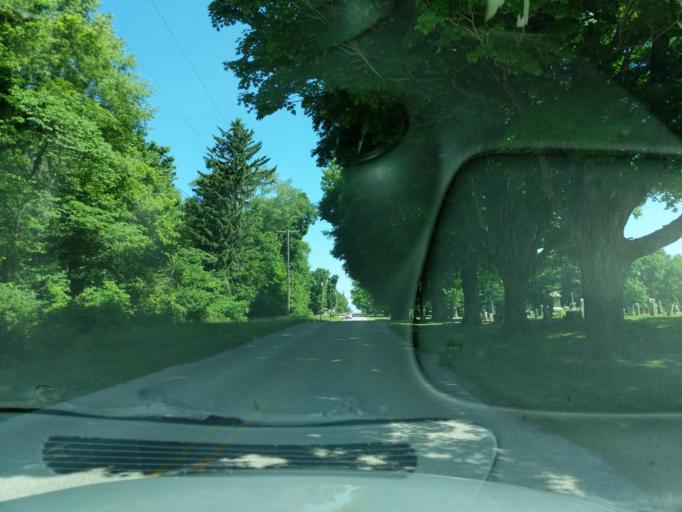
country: US
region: Indiana
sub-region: Huntington County
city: Warren
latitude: 40.7466
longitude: -85.5070
